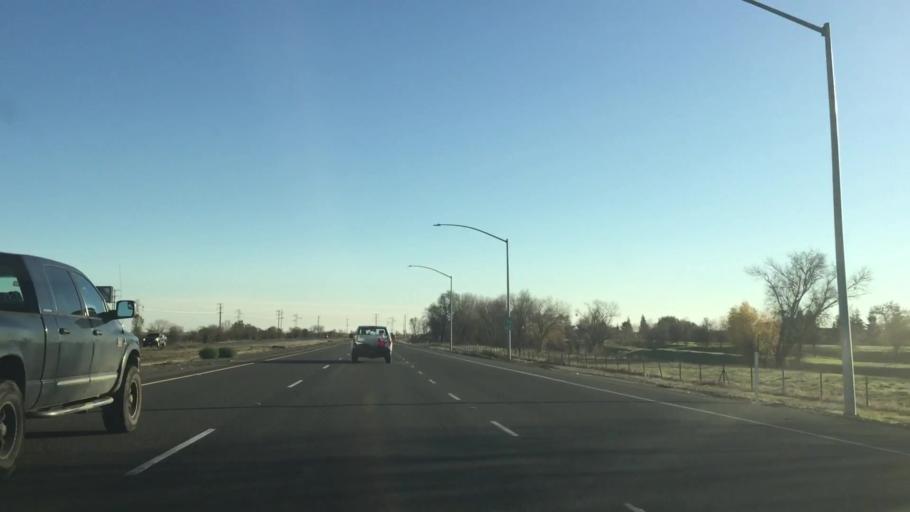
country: US
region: California
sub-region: Yuba County
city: Plumas Lake
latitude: 39.0187
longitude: -121.5457
